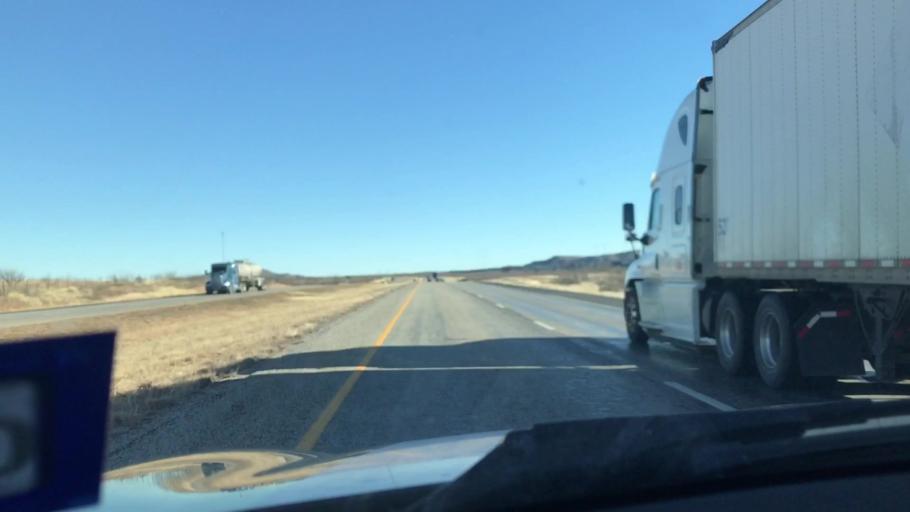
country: US
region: Texas
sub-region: Garza County
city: Post
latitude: 32.9923
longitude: -101.1448
